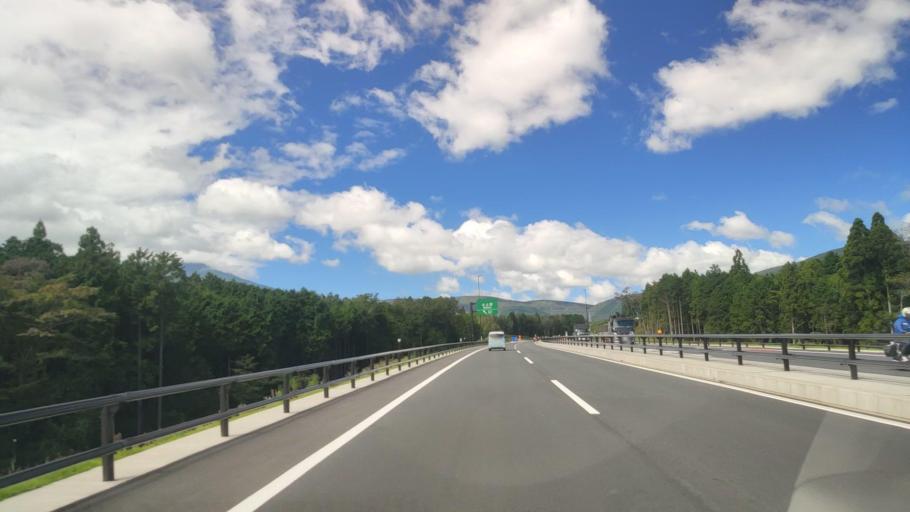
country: JP
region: Shizuoka
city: Gotemba
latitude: 35.3338
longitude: 138.8944
